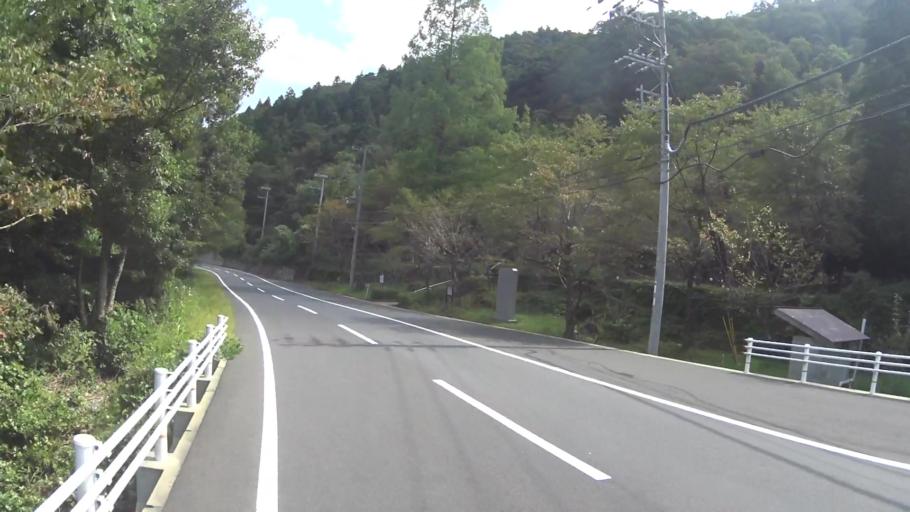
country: JP
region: Kyoto
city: Miyazu
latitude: 35.7079
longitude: 135.2419
